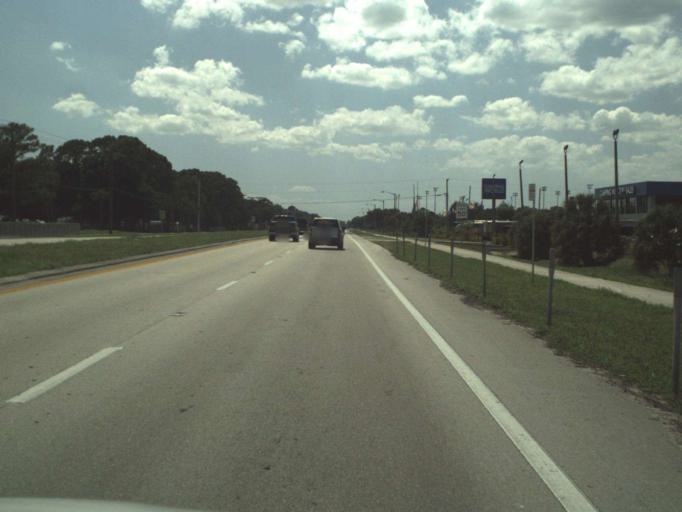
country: US
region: Florida
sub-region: Brevard County
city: Cocoa West
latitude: 28.3599
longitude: -80.7980
